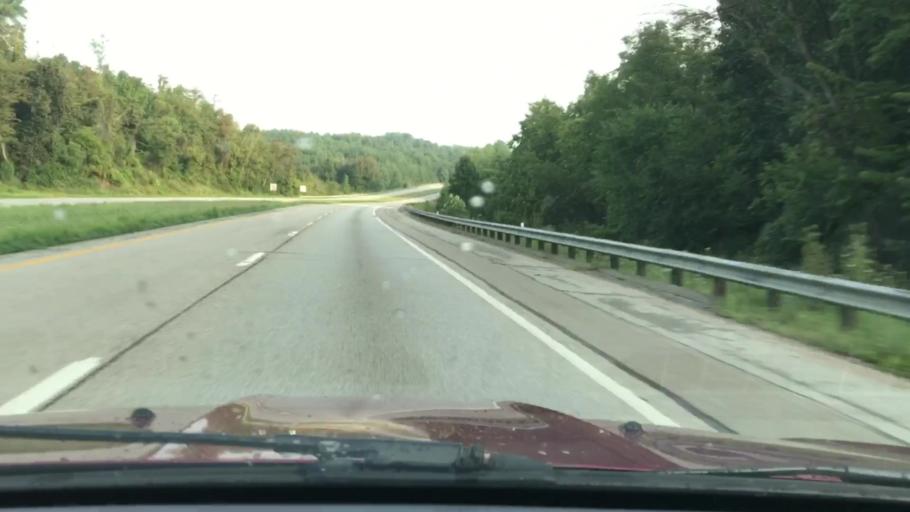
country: US
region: Ohio
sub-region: Washington County
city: Marietta
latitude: 39.4443
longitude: -81.4350
